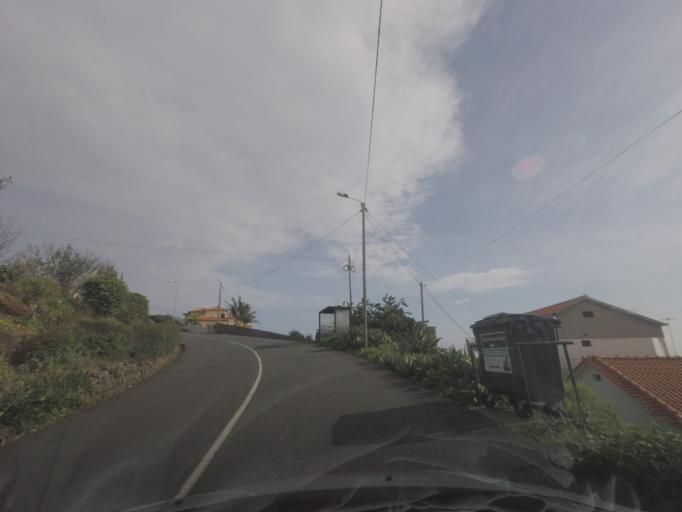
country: PT
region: Madeira
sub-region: Calheta
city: Estreito da Calheta
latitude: 32.7348
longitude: -17.1895
